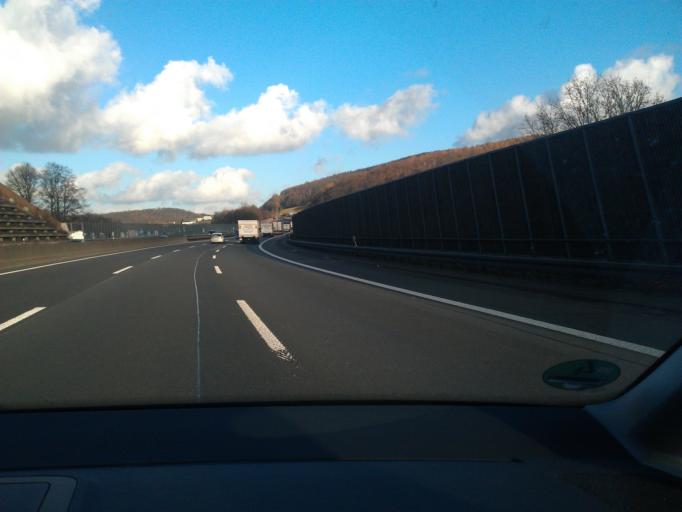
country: DE
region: North Rhine-Westphalia
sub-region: Regierungsbezirk Dusseldorf
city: Wuppertal
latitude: 51.2552
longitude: 7.2282
